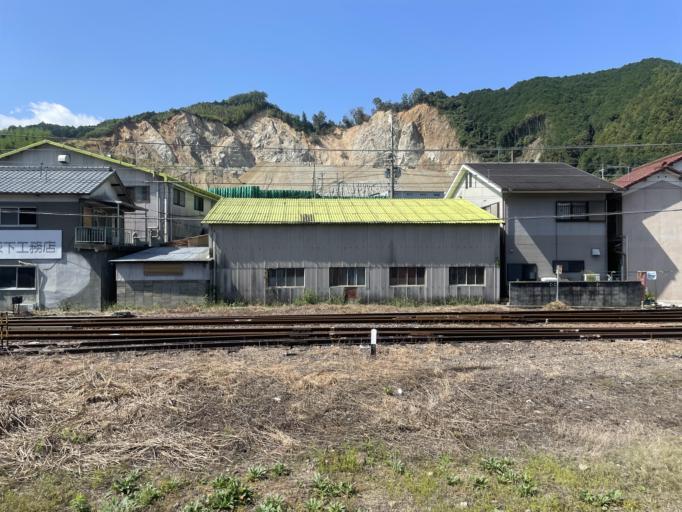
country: JP
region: Nara
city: Gose
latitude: 34.4194
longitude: 135.7502
